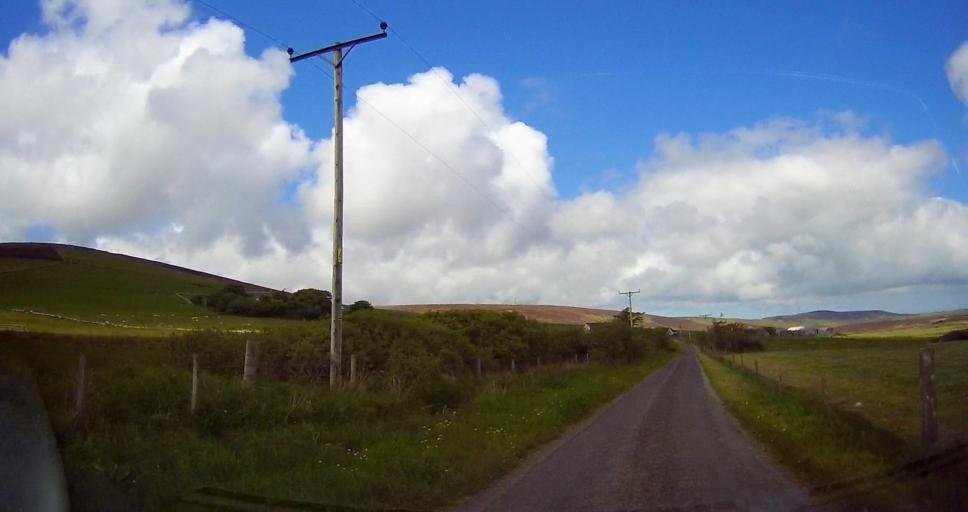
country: GB
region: Scotland
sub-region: Orkney Islands
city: Orkney
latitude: 59.0523
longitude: -3.1042
